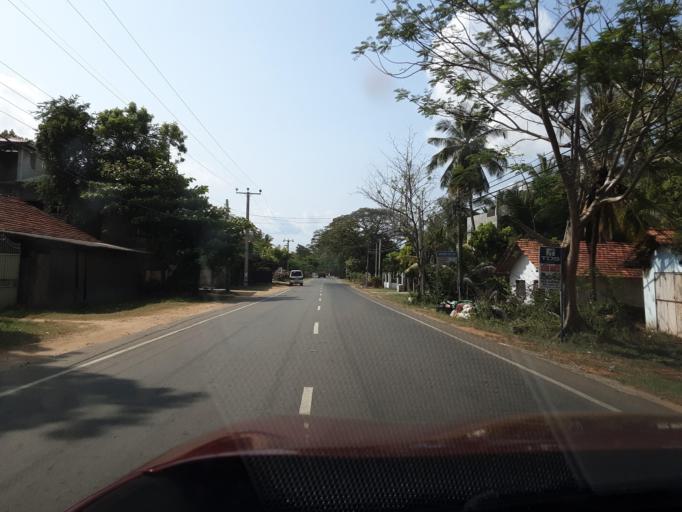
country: LK
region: Southern
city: Tangalla
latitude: 6.3075
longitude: 81.2329
